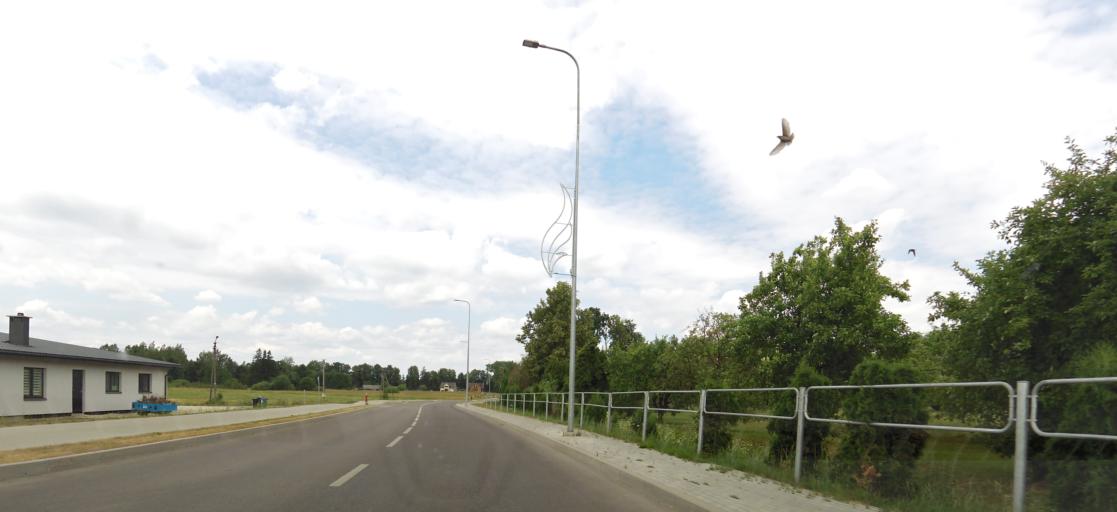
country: LT
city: Sirvintos
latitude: 55.0420
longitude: 24.9681
